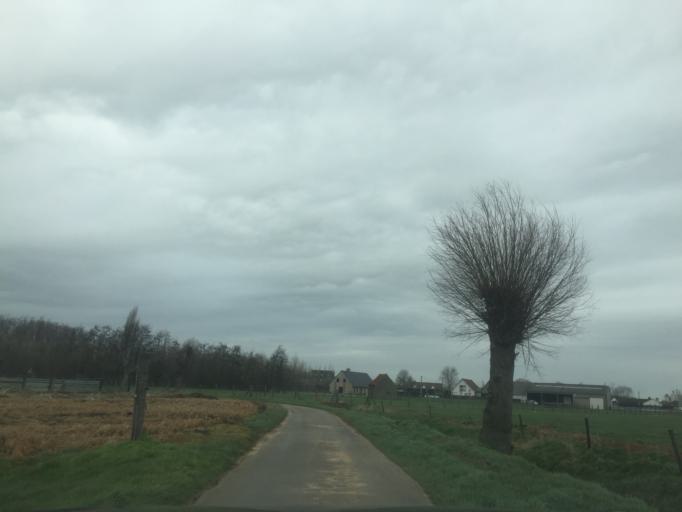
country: BE
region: Flanders
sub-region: Provincie West-Vlaanderen
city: Oostrozebeke
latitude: 50.9162
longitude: 3.3480
